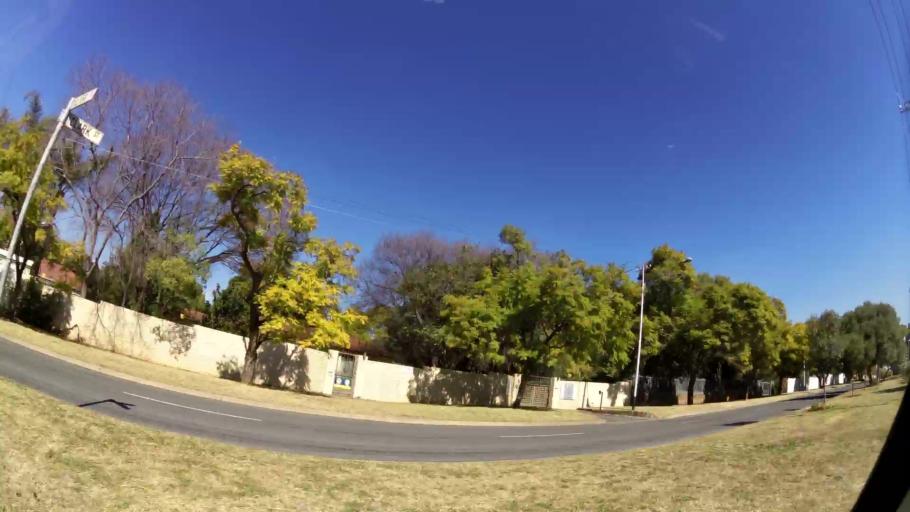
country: ZA
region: Gauteng
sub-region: City of Tshwane Metropolitan Municipality
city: Pretoria
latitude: -25.7729
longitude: 28.2477
